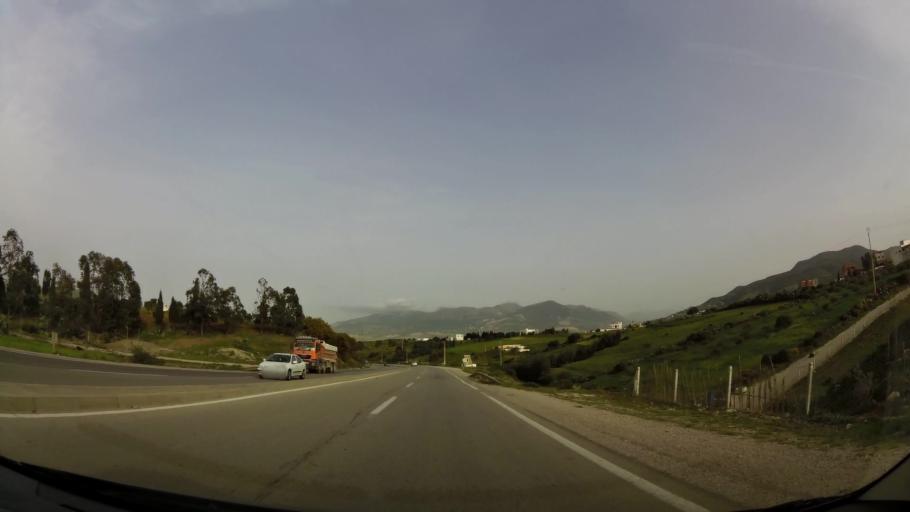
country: MA
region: Tanger-Tetouan
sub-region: Tetouan
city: Saddina
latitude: 35.5610
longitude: -5.4796
